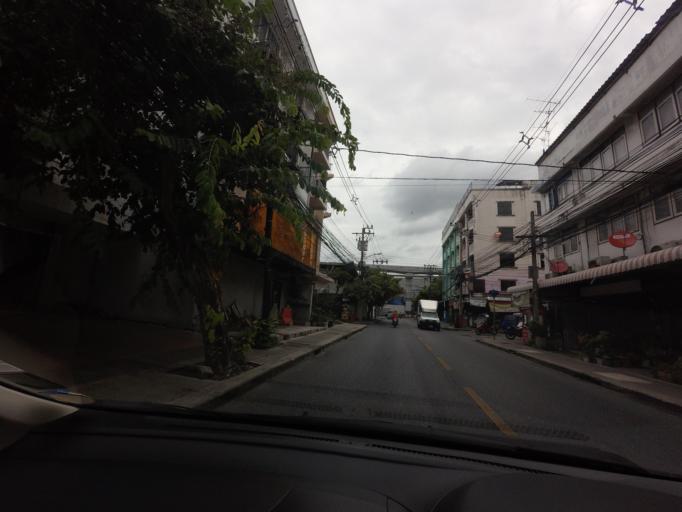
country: TH
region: Bangkok
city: Wang Thonglang
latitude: 13.7770
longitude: 100.6239
